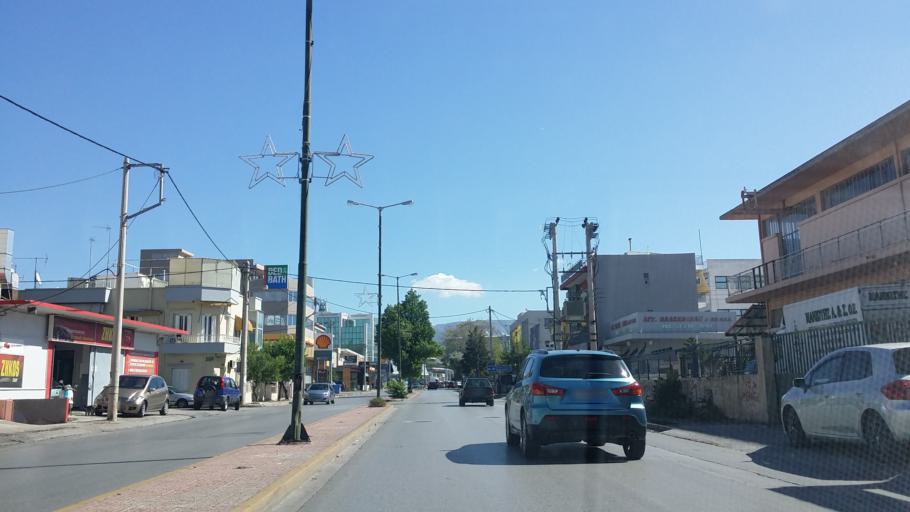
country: GR
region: Attica
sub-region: Nomarchia Athinas
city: Peristeri
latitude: 38.0103
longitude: 23.7115
